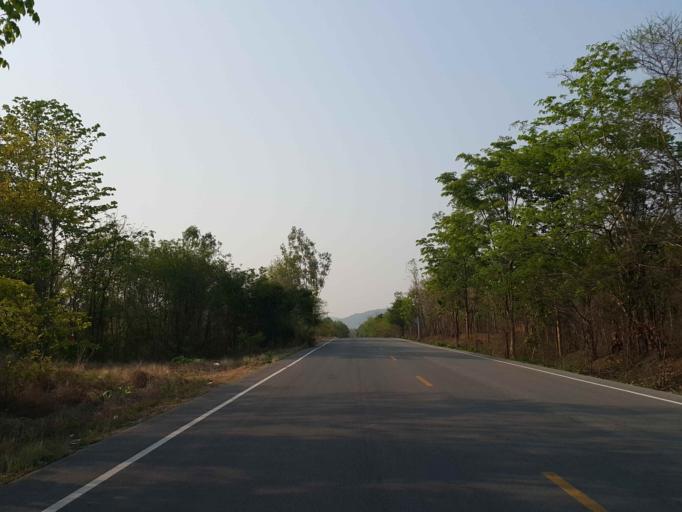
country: TH
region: Sukhothai
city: Thung Saliam
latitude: 17.3553
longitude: 99.4137
